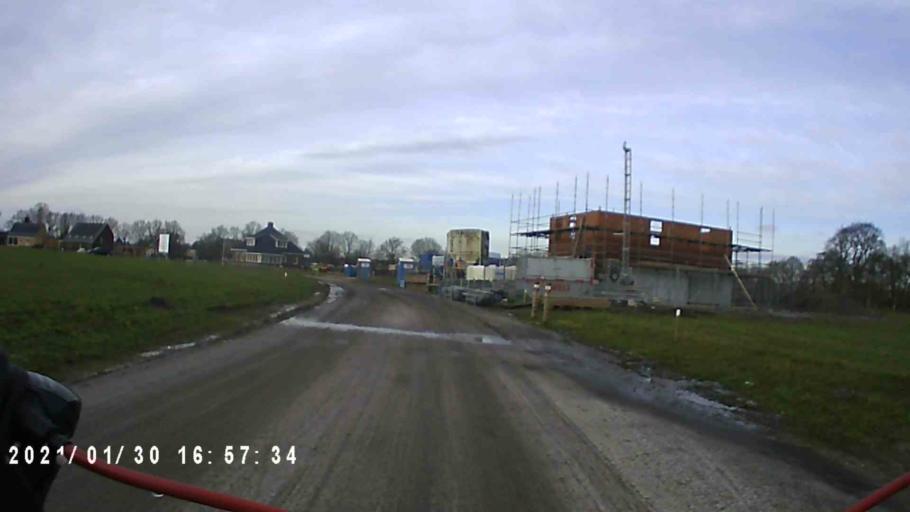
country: NL
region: Groningen
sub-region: Gemeente Leek
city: Leek
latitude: 53.1508
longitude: 6.3798
